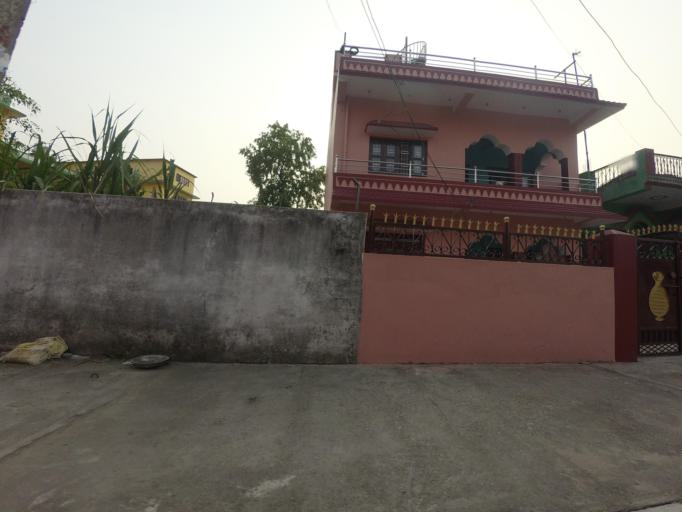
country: NP
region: Western Region
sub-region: Lumbini Zone
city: Bhairahawa
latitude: 27.5082
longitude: 83.4473
